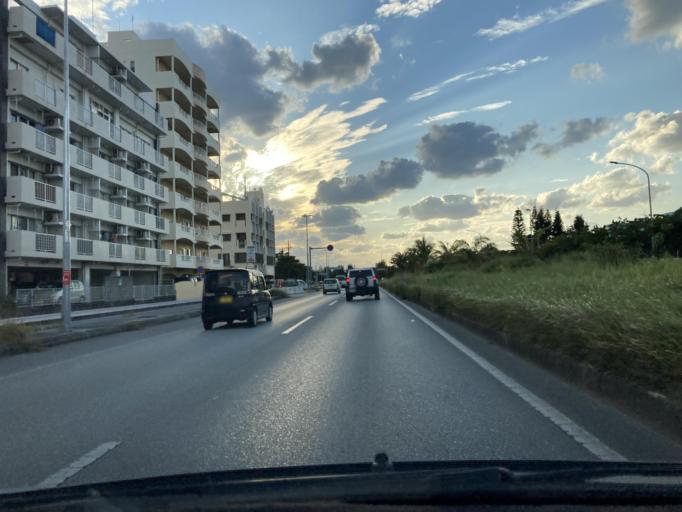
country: JP
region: Okinawa
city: Ginowan
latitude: 26.2791
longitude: 127.7362
